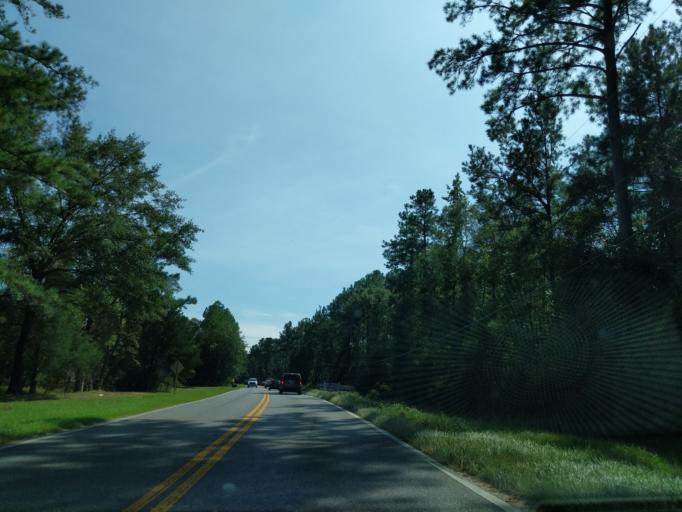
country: US
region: Florida
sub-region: Okaloosa County
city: Crestview
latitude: 30.7361
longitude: -86.6233
